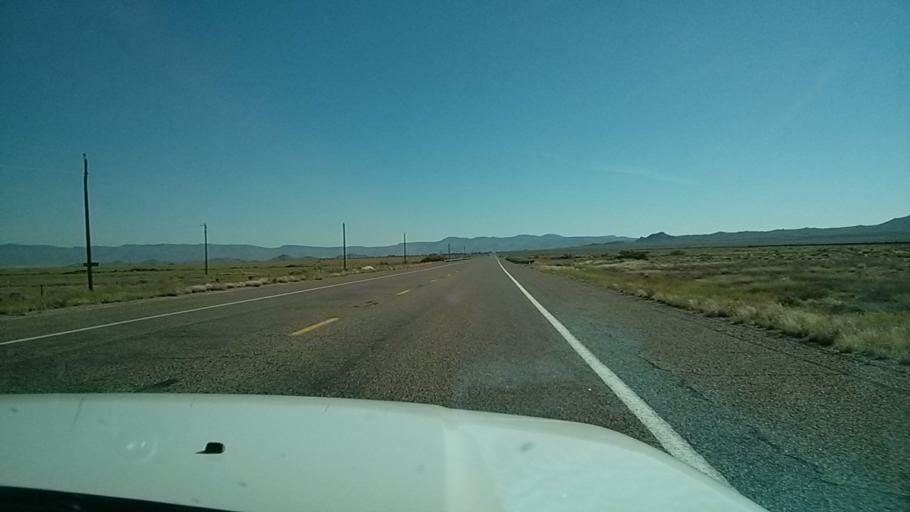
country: US
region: Arizona
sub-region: Mohave County
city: New Kingman-Butler
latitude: 35.3527
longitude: -113.8811
